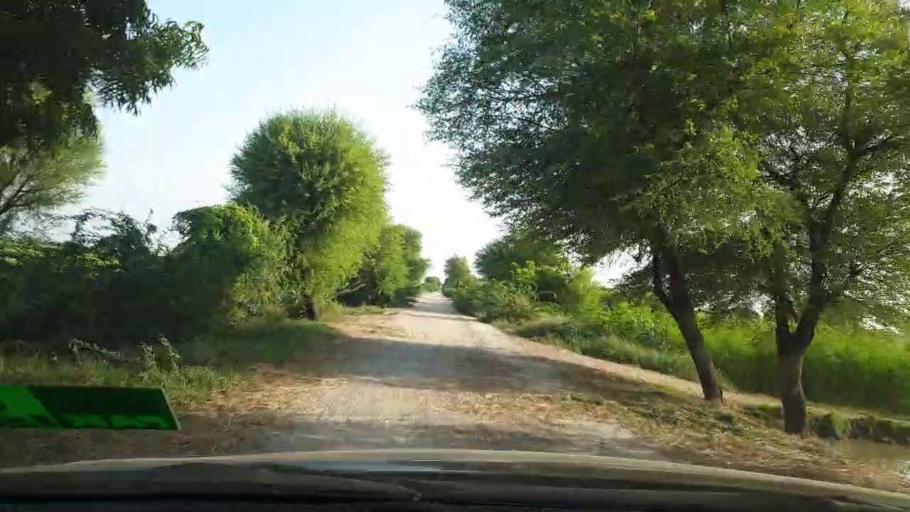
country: PK
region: Sindh
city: Naukot
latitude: 24.7347
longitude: 69.2258
